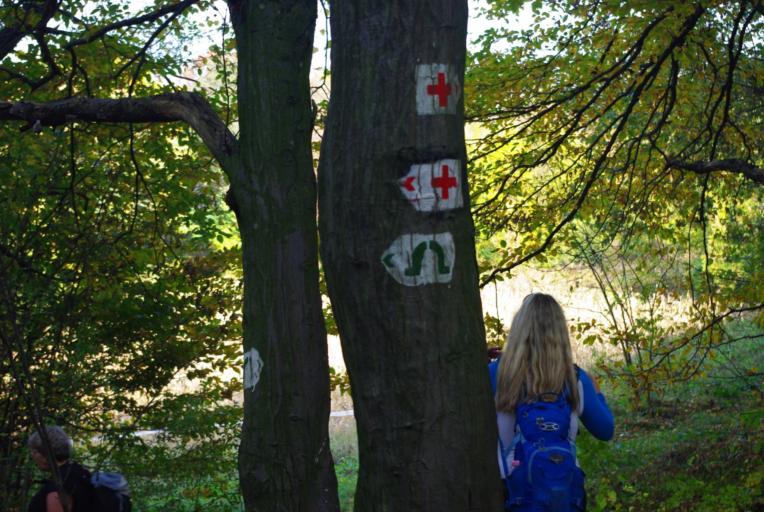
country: HU
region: Gyor-Moson-Sopron
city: Bakonyszentlaszlo
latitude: 47.3526
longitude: 17.8781
